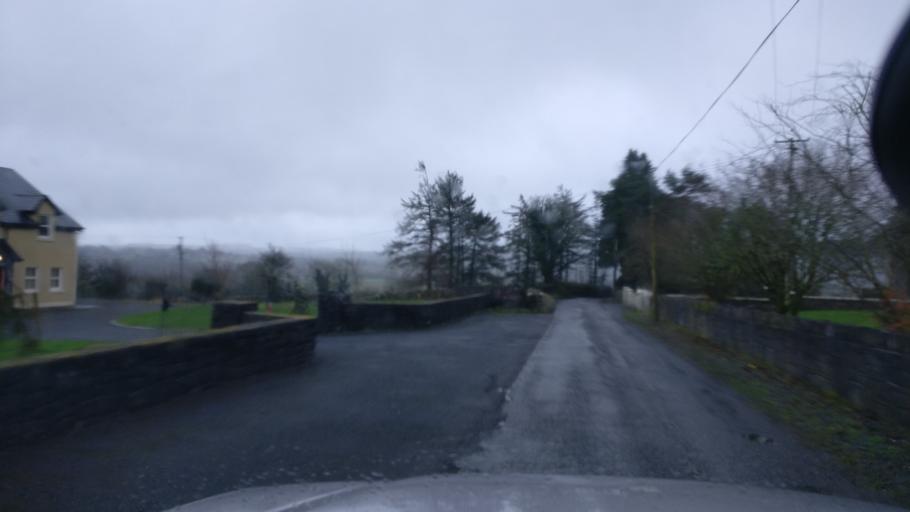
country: IE
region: Connaught
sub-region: County Galway
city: Loughrea
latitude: 53.1685
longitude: -8.6445
